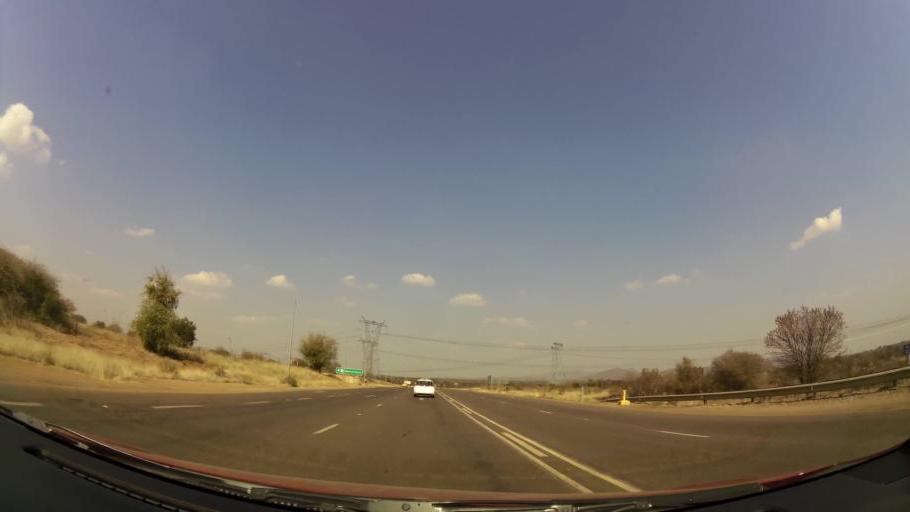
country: ZA
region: North-West
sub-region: Bojanala Platinum District Municipality
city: Mogwase
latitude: -25.3883
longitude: 27.0695
